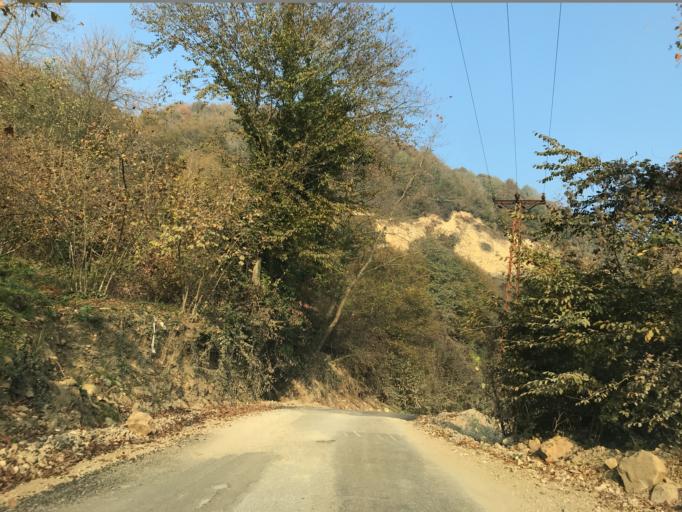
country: TR
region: Duzce
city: Cumayeri
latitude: 40.9211
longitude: 30.9289
